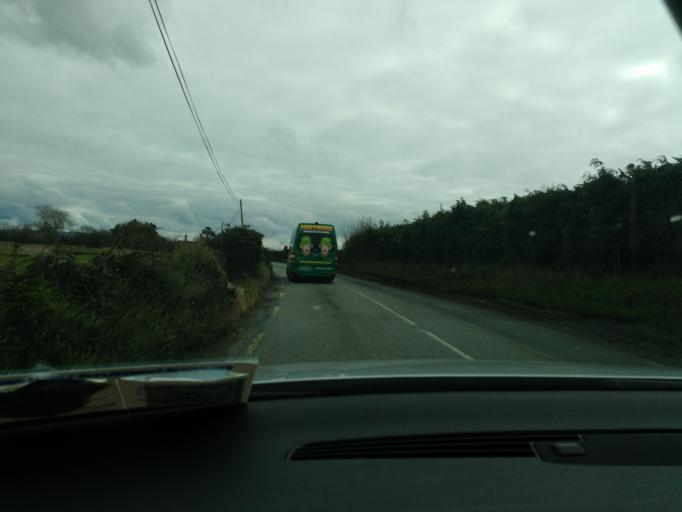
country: IE
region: Leinster
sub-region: Kilkenny
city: Ballyragget
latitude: 52.7300
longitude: -7.3854
